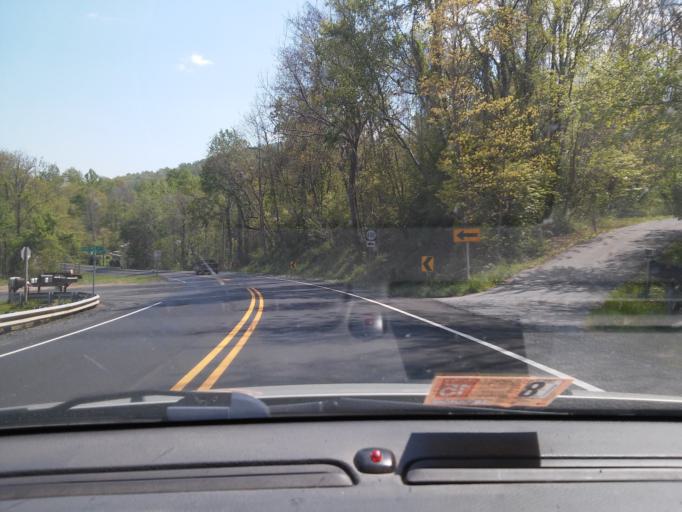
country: US
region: Virginia
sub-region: Warren County
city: Apple Mountain Lake
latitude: 38.8443
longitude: -78.1255
